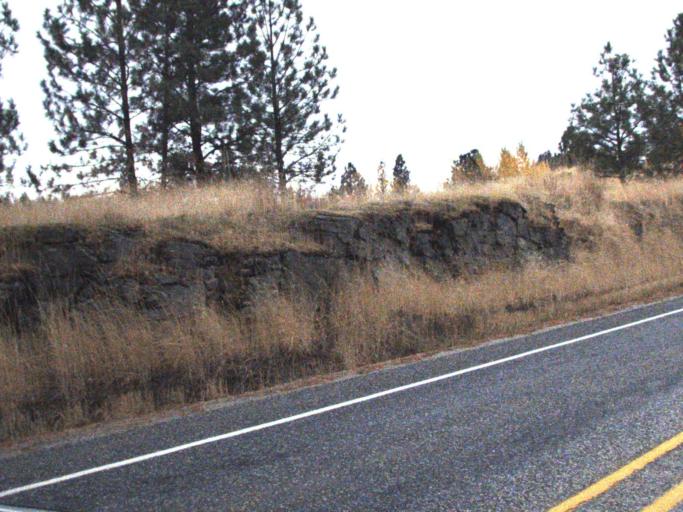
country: US
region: Washington
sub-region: Stevens County
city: Kettle Falls
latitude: 48.6570
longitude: -118.1137
